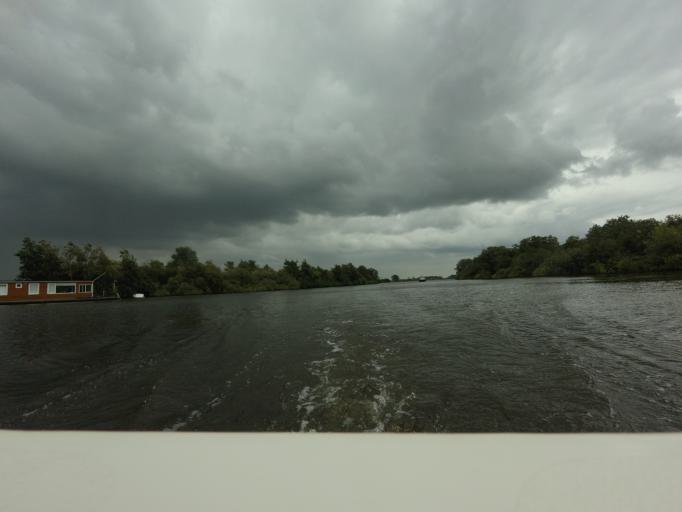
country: NL
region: Friesland
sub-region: Gemeente Tytsjerksteradiel
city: Garyp
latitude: 53.1223
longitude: 5.9429
